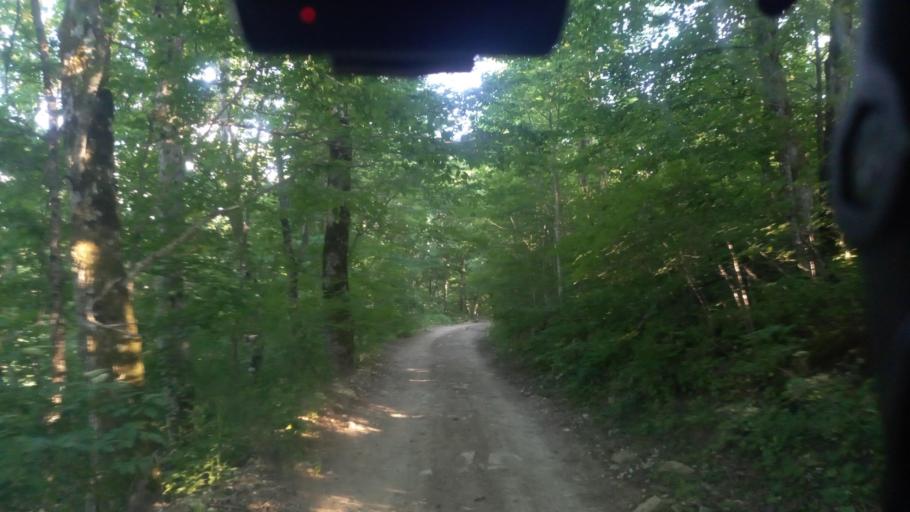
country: RU
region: Krasnodarskiy
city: Gelendzhik
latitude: 44.6256
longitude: 38.1889
